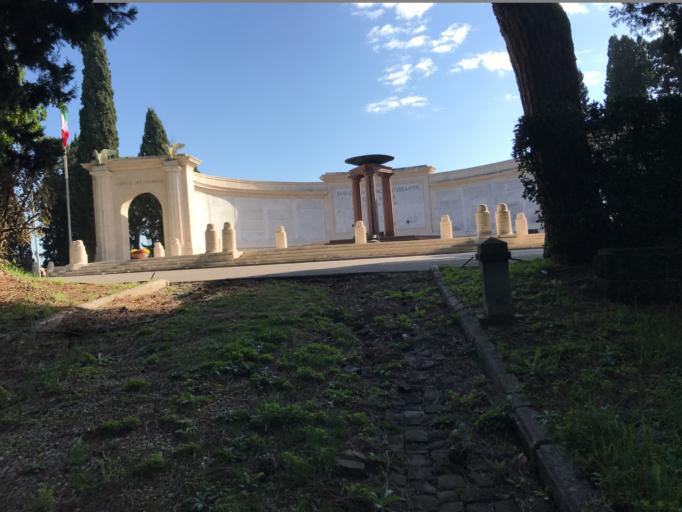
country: IT
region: Latium
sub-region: Citta metropolitana di Roma Capitale
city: Rome
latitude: 41.9039
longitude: 12.5311
